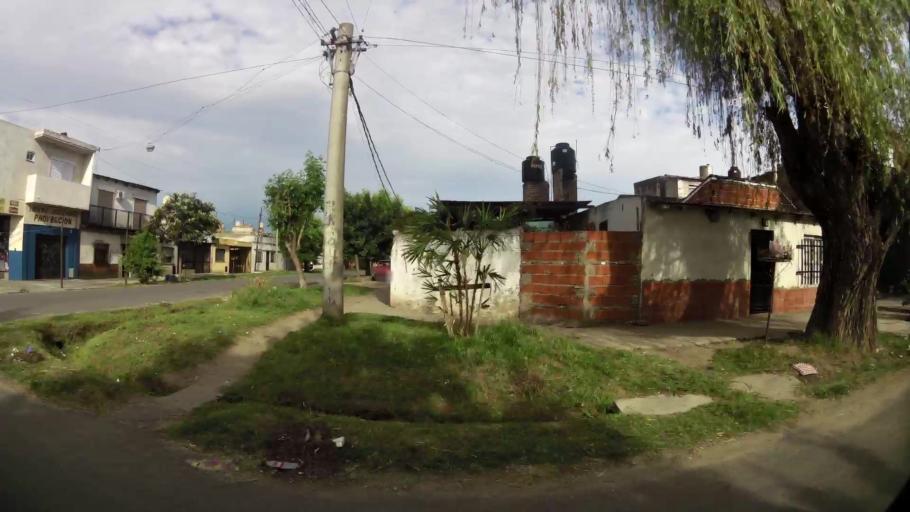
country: AR
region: Santa Fe
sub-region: Departamento de Rosario
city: Rosario
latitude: -32.9747
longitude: -60.6852
